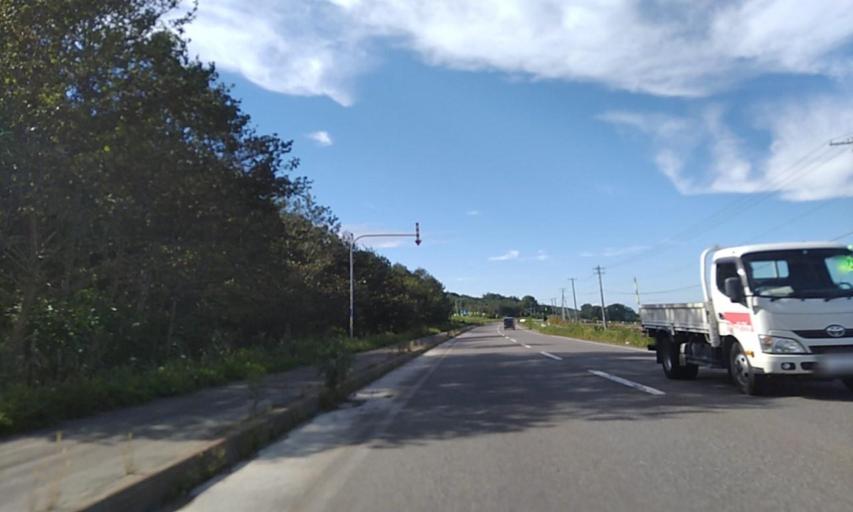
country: JP
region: Hokkaido
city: Obihiro
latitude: 42.8203
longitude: 143.4815
